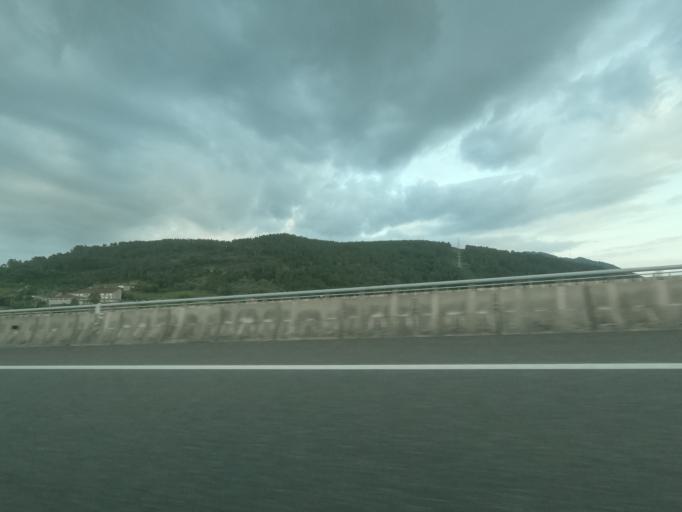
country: ES
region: Galicia
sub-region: Provincia de Ourense
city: Ribadavia
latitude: 42.3016
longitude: -8.1335
